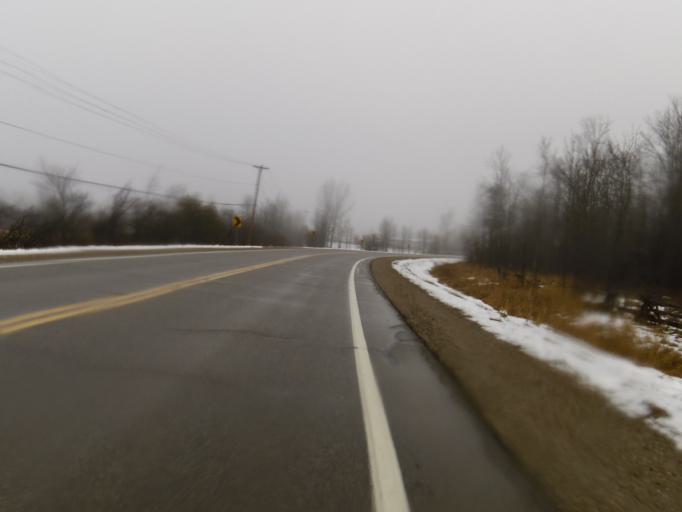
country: CA
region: Ontario
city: Perth
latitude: 44.8258
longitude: -76.3909
